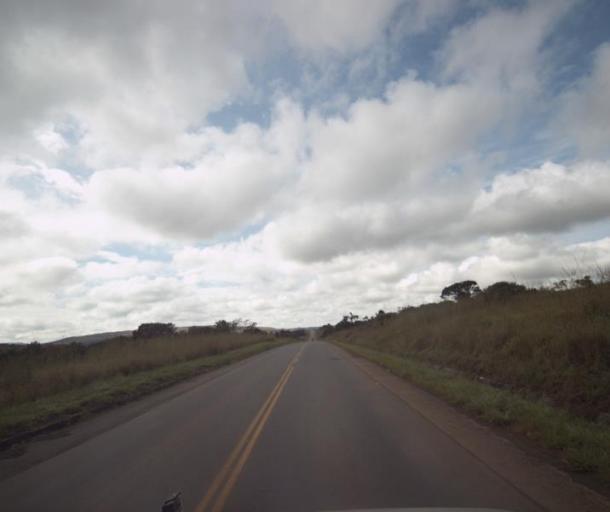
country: BR
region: Goias
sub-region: Pirenopolis
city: Pirenopolis
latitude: -15.8347
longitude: -48.7784
